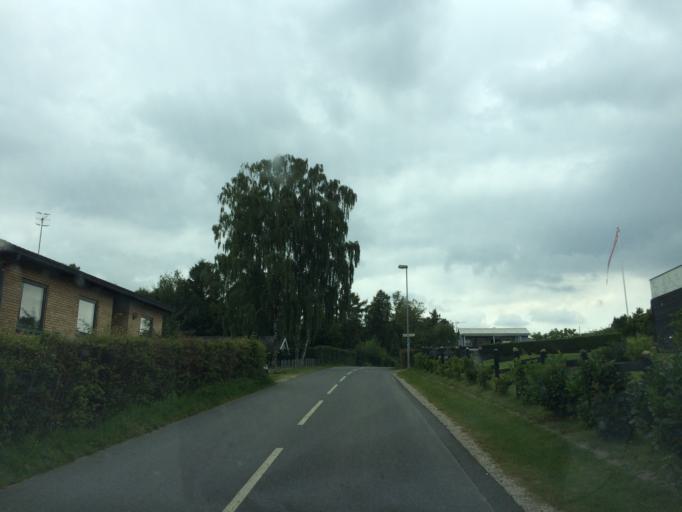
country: DK
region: Central Jutland
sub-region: Syddjurs Kommune
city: Ebeltoft
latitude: 56.2308
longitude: 10.6113
